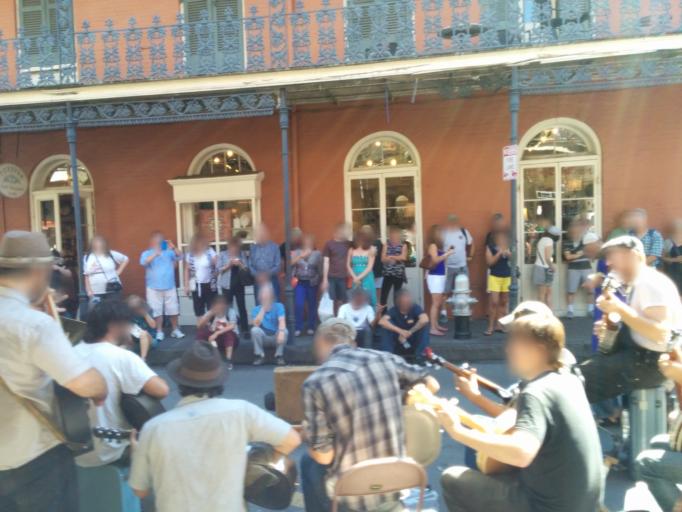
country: US
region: Louisiana
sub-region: Orleans Parish
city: New Orleans
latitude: 29.9581
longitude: -90.0647
